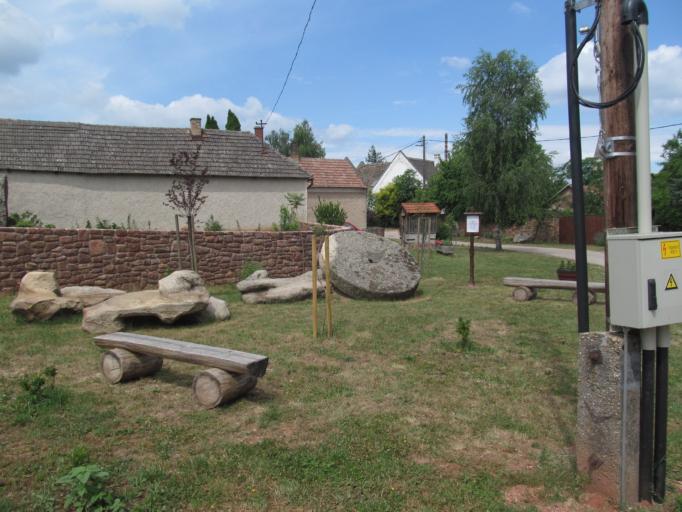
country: HU
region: Veszprem
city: Revfueloep
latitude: 46.8482
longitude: 17.6035
